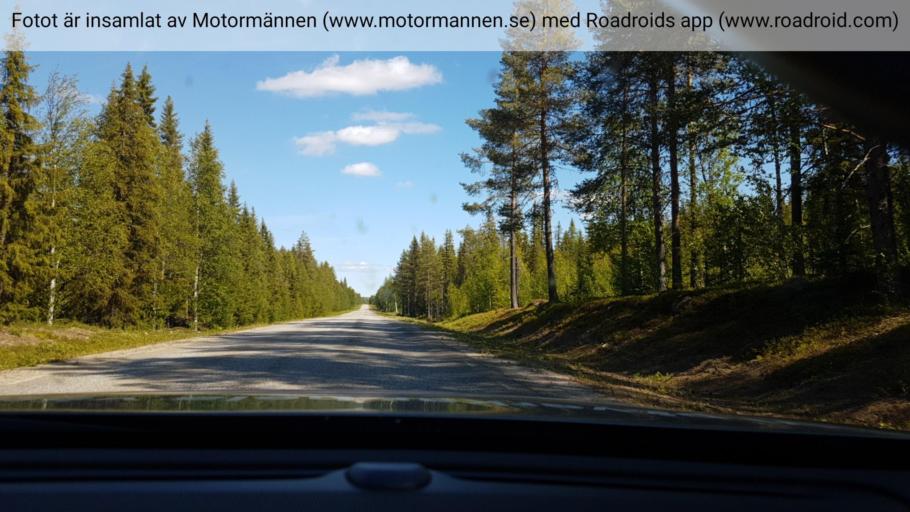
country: SE
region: Vaesterbotten
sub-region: Lycksele Kommun
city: Soderfors
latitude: 64.6335
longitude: 17.9383
